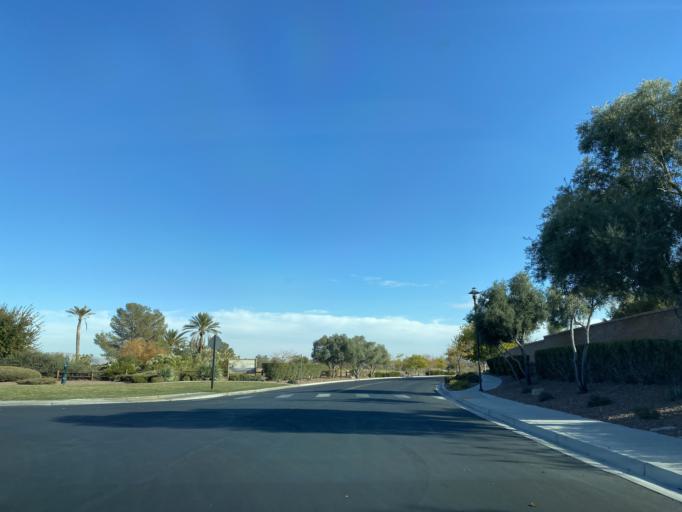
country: US
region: Nevada
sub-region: Clark County
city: North Las Vegas
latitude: 36.3185
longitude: -115.2522
